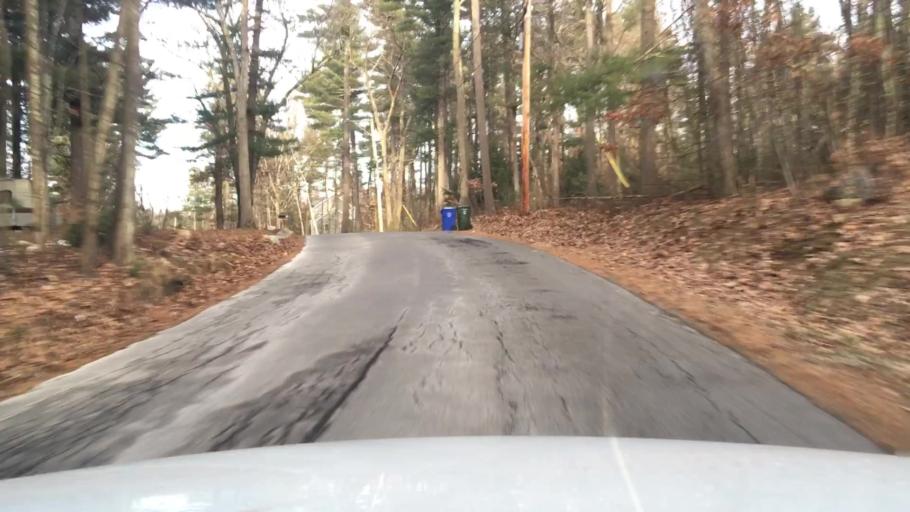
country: US
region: New Hampshire
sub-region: Rockingham County
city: Londonderry
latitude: 42.8923
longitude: -71.4055
